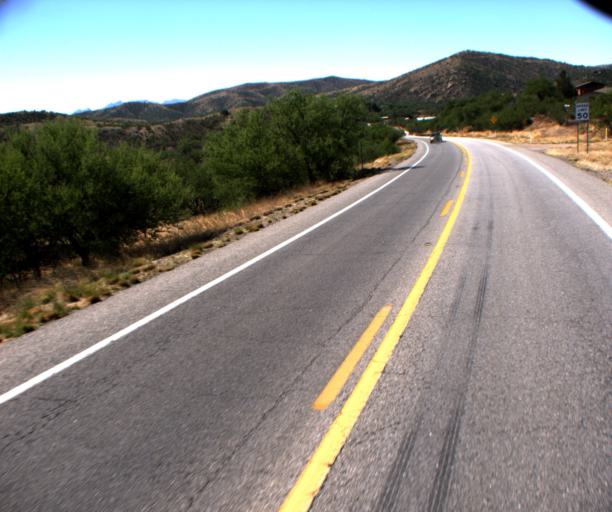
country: US
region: Arizona
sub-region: Santa Cruz County
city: Nogales
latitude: 31.3996
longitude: -110.8698
